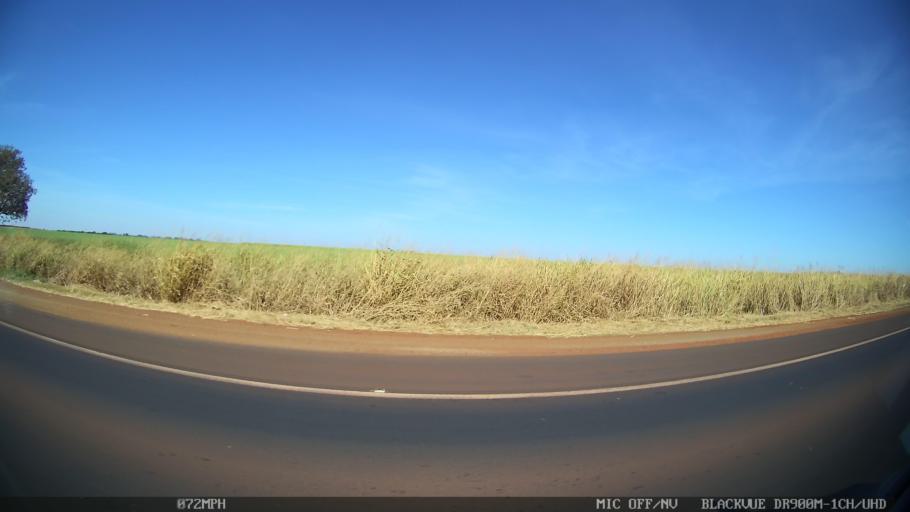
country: BR
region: Sao Paulo
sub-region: Barretos
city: Barretos
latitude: -20.4787
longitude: -48.4999
